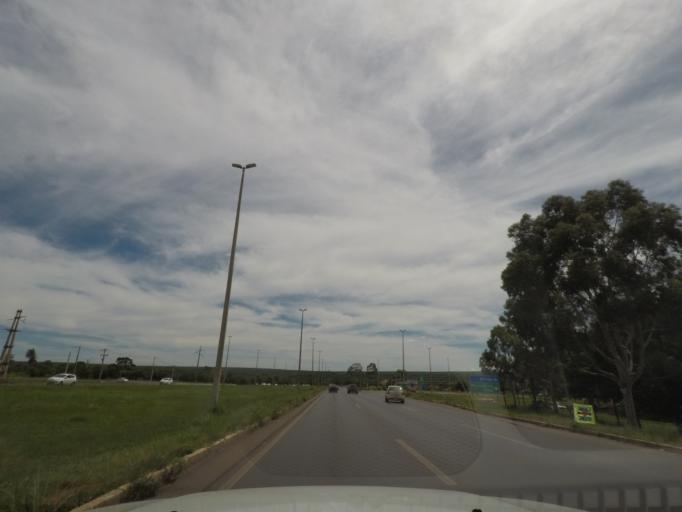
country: BR
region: Goias
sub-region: Planaltina
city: Planaltina
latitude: -15.5989
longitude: -47.6765
